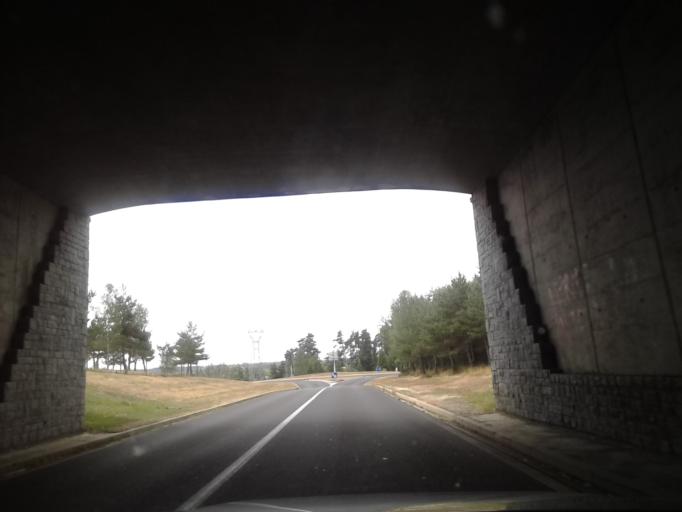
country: FR
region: Languedoc-Roussillon
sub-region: Departement de la Lozere
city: Le Malzieu-Ville
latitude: 44.8693
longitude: 3.2521
